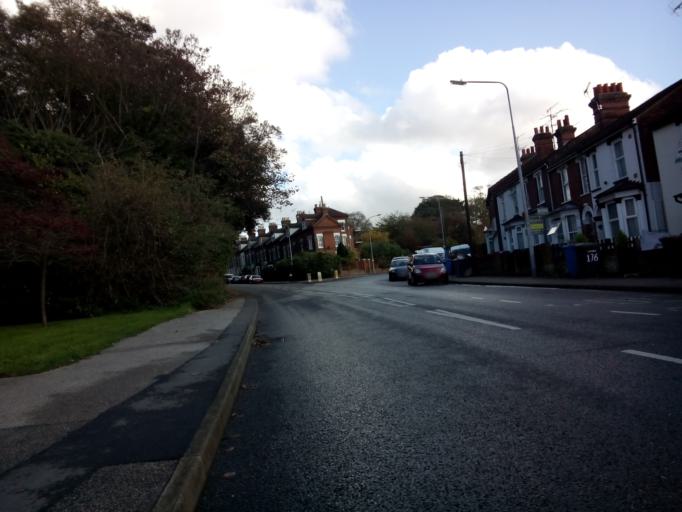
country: GB
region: England
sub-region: Suffolk
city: Ipswich
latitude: 52.0580
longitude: 1.1770
